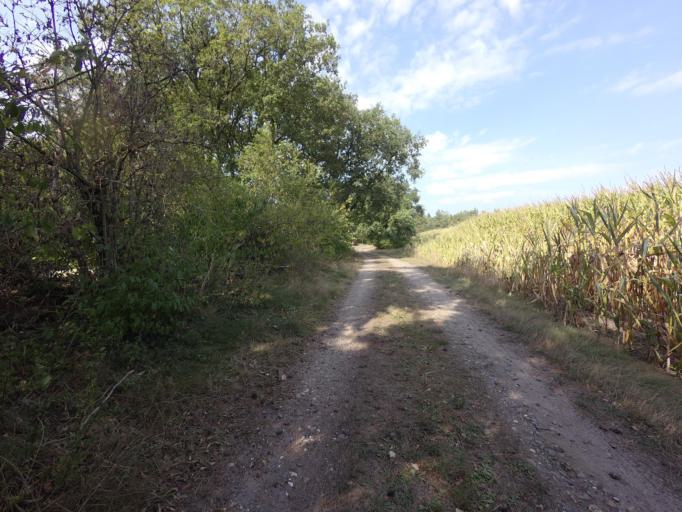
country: NL
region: North Brabant
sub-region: Gemeente Someren
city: Someren
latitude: 51.3892
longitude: 5.6665
